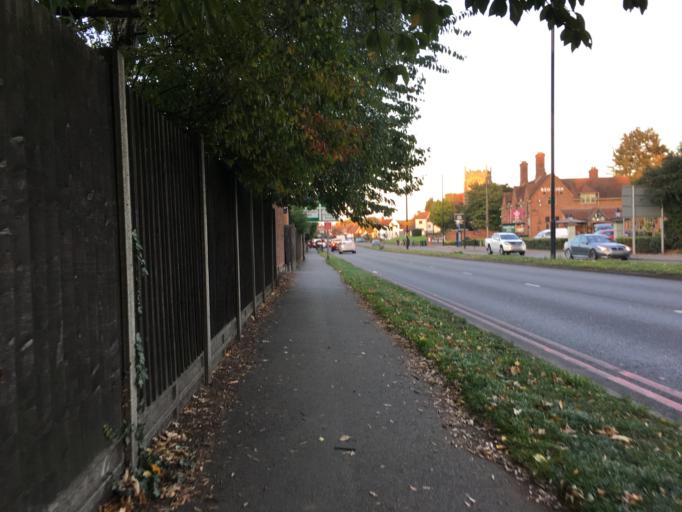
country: GB
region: England
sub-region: Warwickshire
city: Exhall
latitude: 52.4240
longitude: -1.4460
